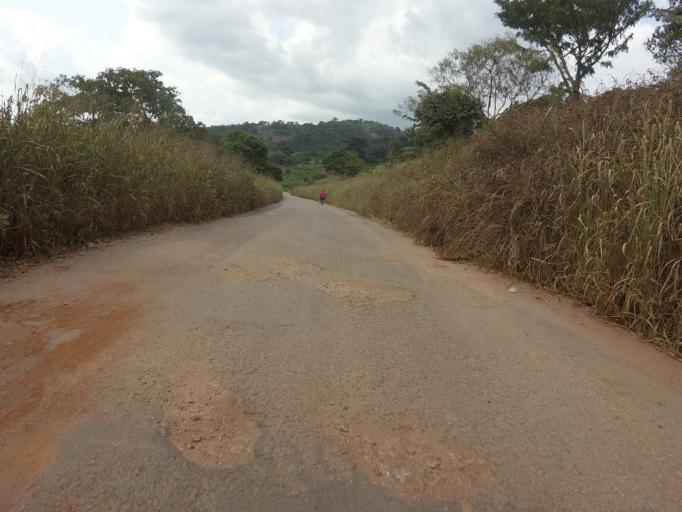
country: GH
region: Volta
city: Ho
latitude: 6.6839
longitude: 0.3483
